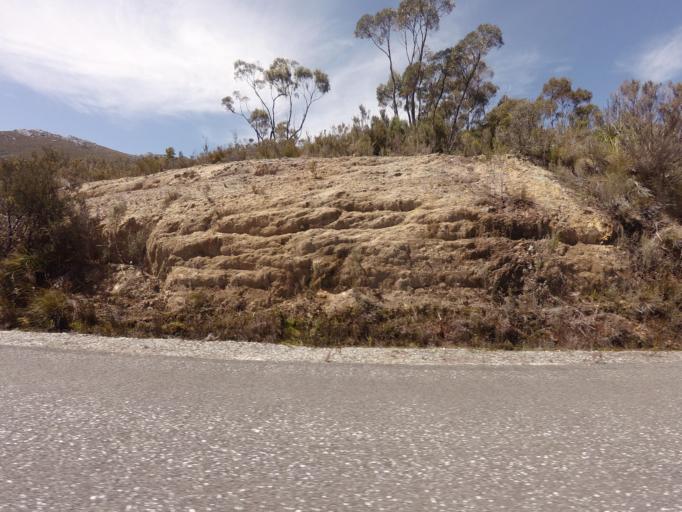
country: AU
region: Tasmania
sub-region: West Coast
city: Queenstown
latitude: -42.7781
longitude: 146.0573
